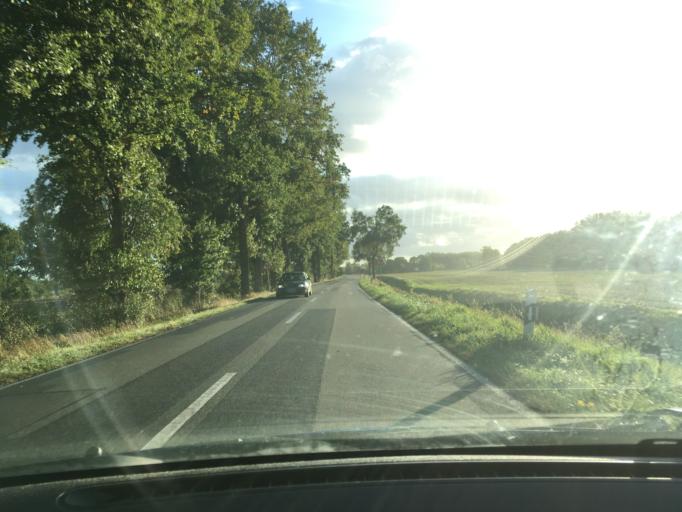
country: DE
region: Lower Saxony
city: Hittbergen
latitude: 53.3358
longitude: 10.6023
